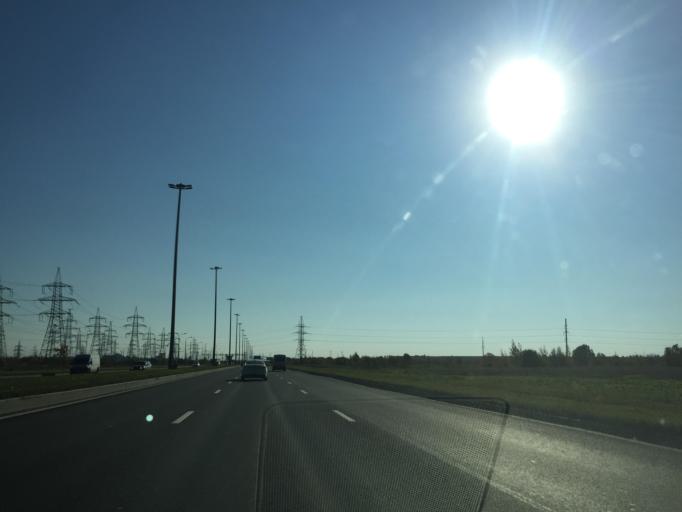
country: RU
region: St.-Petersburg
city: Petro-Slavyanka
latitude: 59.7564
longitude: 30.5181
